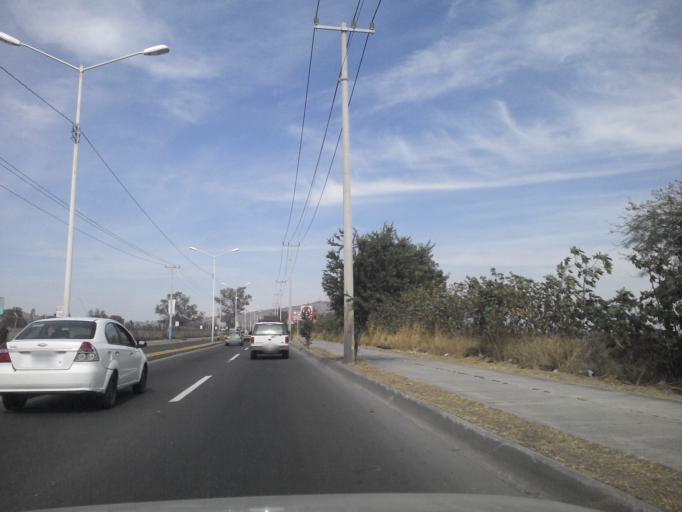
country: MX
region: Jalisco
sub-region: San Pedro Tlaquepaque
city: Paseo del Prado
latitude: 20.5562
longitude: -103.3958
